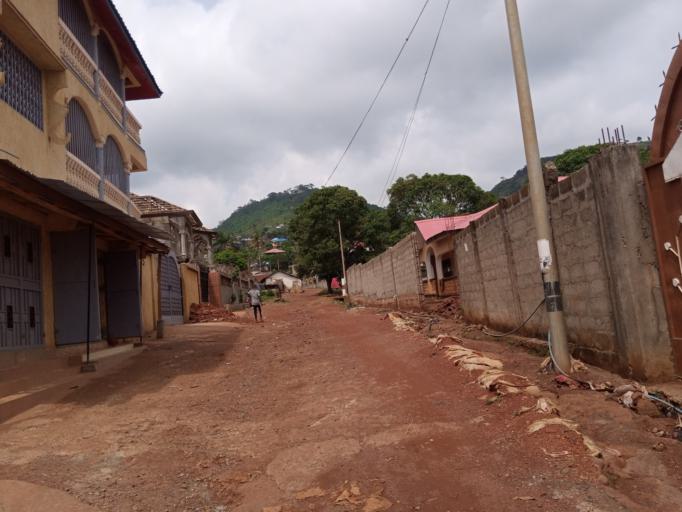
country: SL
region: Western Area
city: Waterloo
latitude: 8.3706
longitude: -13.0959
